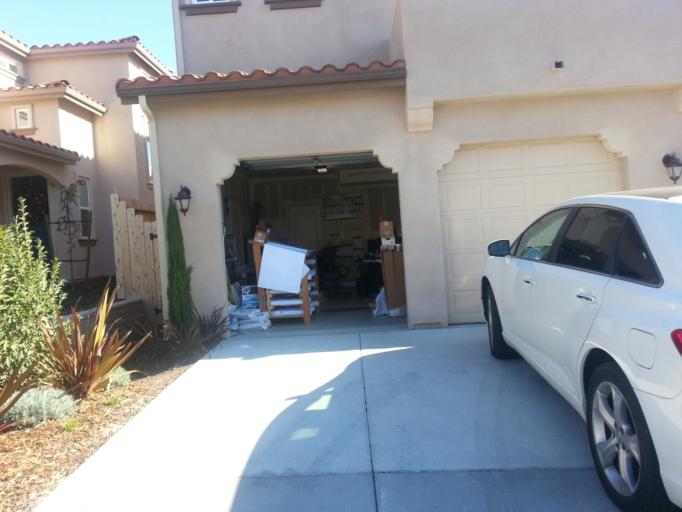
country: US
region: California
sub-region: San Luis Obispo County
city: Grover Beach
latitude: 35.1321
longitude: -120.6089
